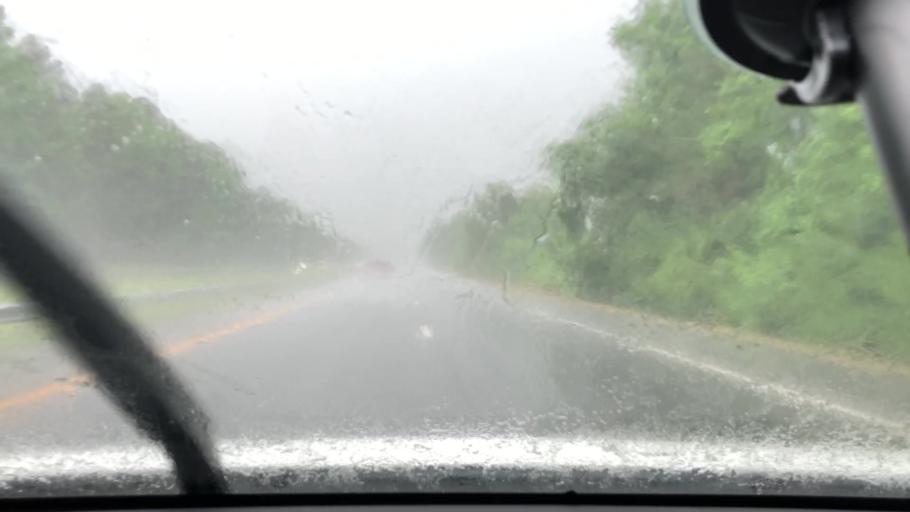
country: US
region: North Carolina
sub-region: Halifax County
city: Halifax
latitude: 36.3415
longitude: -77.6903
